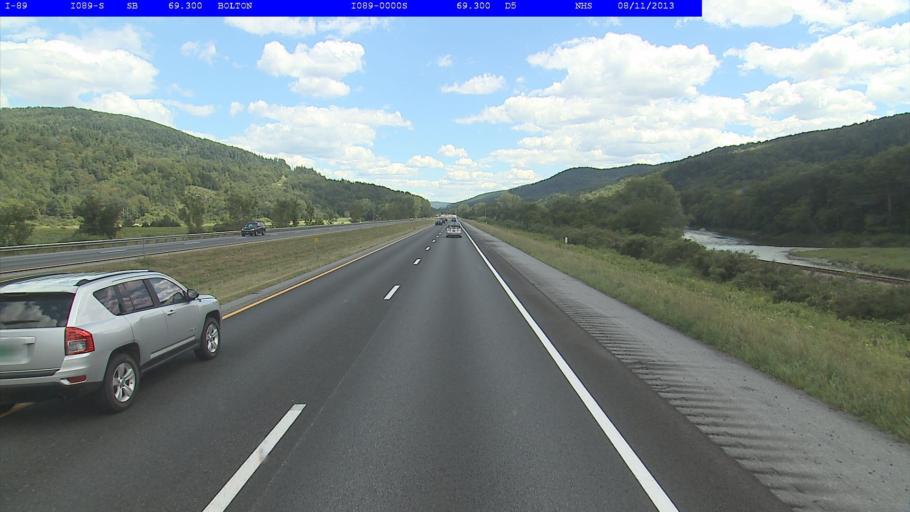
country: US
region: Vermont
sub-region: Washington County
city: Waterbury
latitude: 44.3663
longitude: -72.8551
